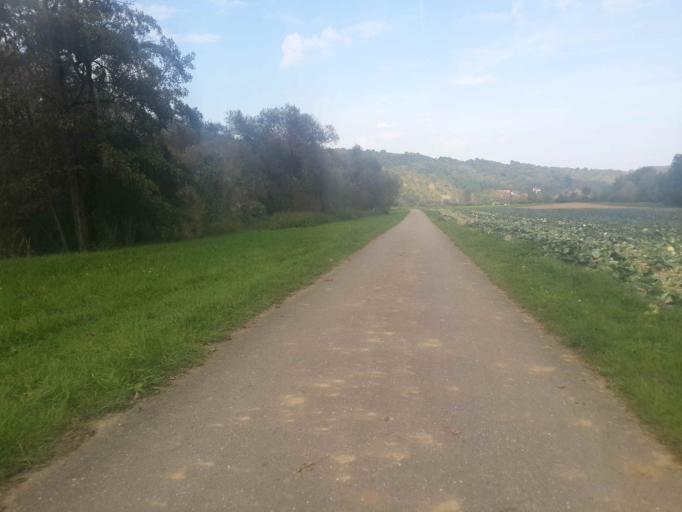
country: DE
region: Baden-Wuerttemberg
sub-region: Regierungsbezirk Stuttgart
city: Widdern
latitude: 49.3031
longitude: 9.4358
